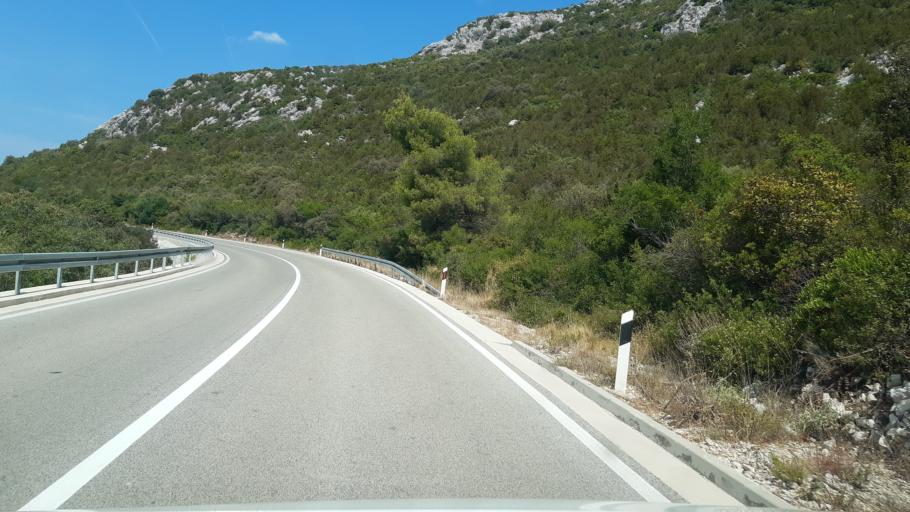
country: HR
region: Dubrovacko-Neretvanska
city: Ston
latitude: 42.8454
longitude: 17.7282
